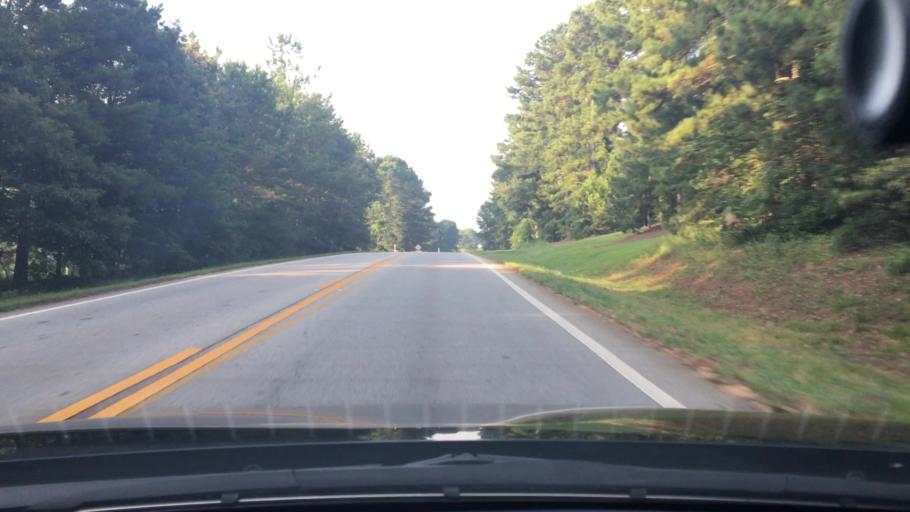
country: US
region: Georgia
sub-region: Fayette County
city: Peachtree City
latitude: 33.3781
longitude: -84.6265
